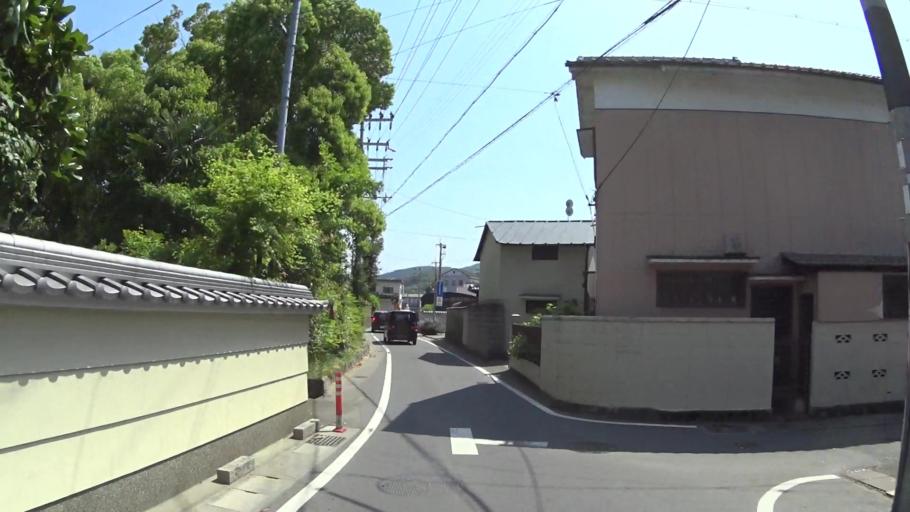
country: JP
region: Kyoto
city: Kameoka
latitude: 35.0236
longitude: 135.5712
